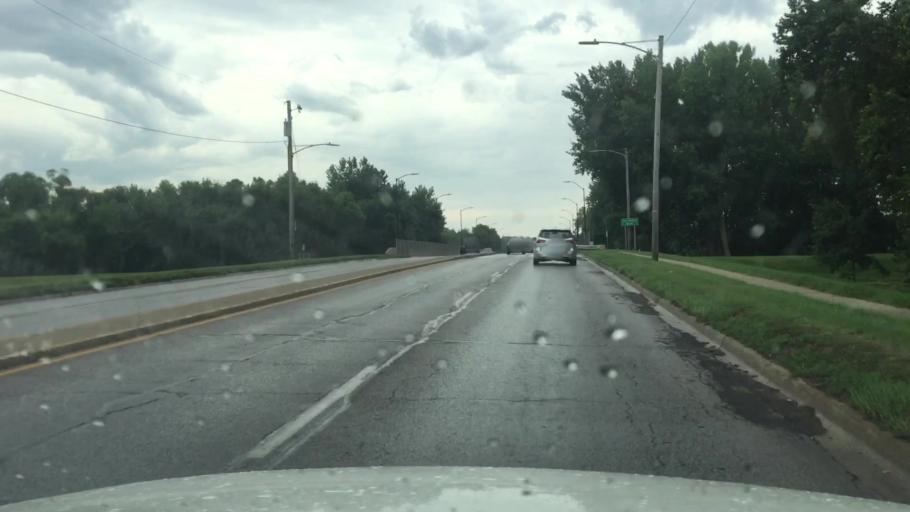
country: US
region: Iowa
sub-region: Polk County
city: Des Moines
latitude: 41.5776
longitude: -93.5970
